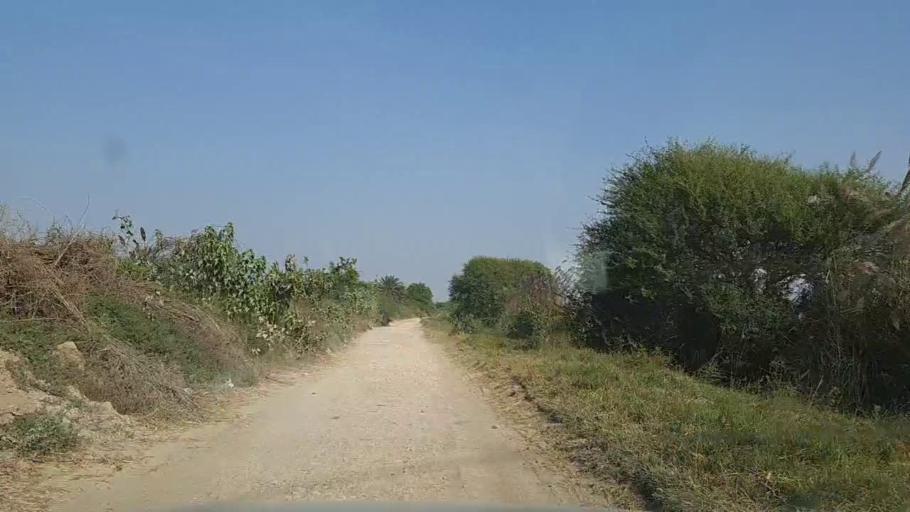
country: PK
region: Sindh
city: Mirpur Sakro
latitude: 24.5575
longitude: 67.5849
